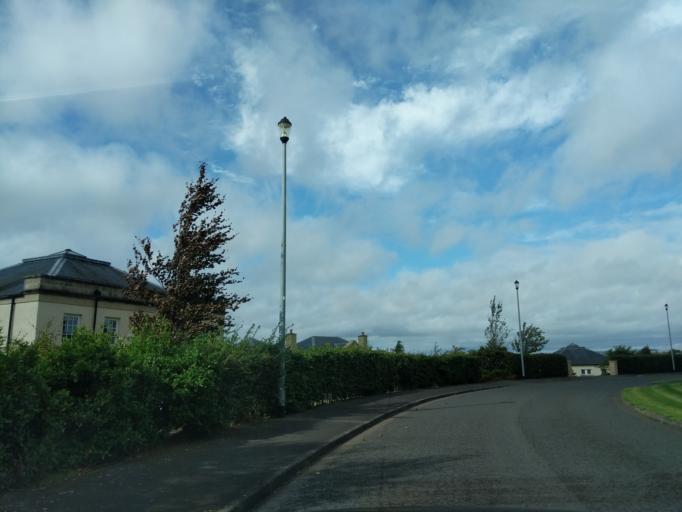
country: GB
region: Scotland
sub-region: The Scottish Borders
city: Kelso
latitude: 55.5636
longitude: -2.4707
